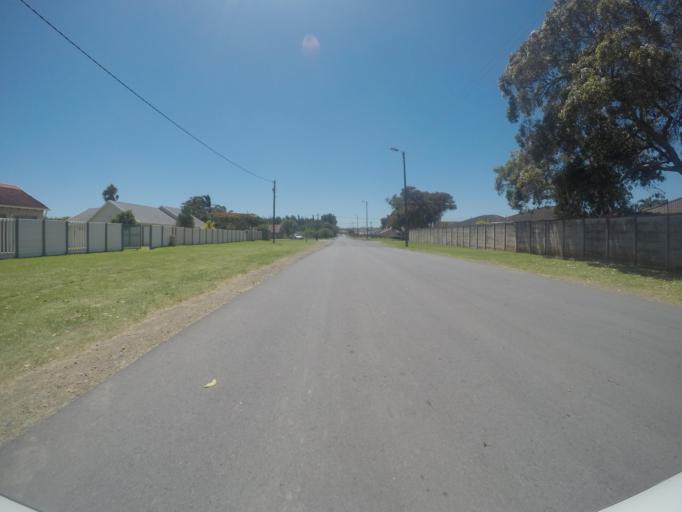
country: ZA
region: Eastern Cape
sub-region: Buffalo City Metropolitan Municipality
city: East London
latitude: -32.9512
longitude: 27.9975
